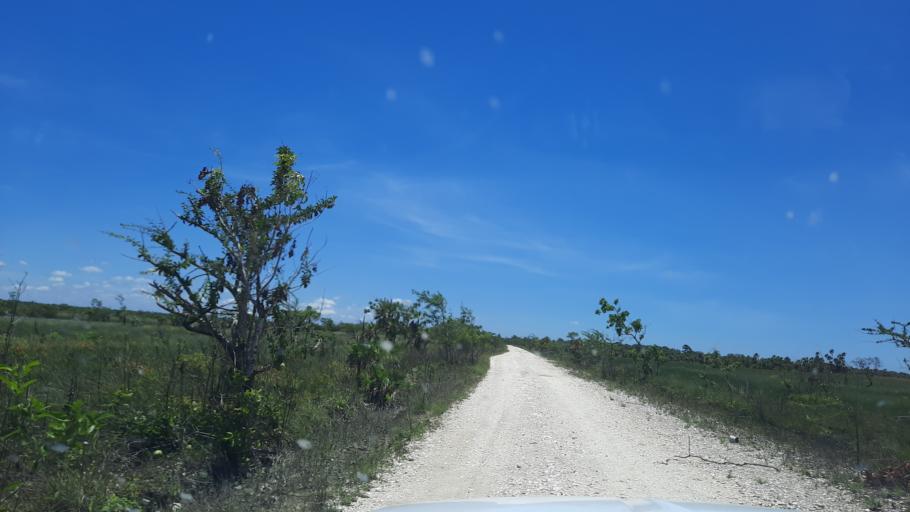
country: BZ
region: Cayo
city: Belmopan
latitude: 17.3906
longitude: -88.4907
